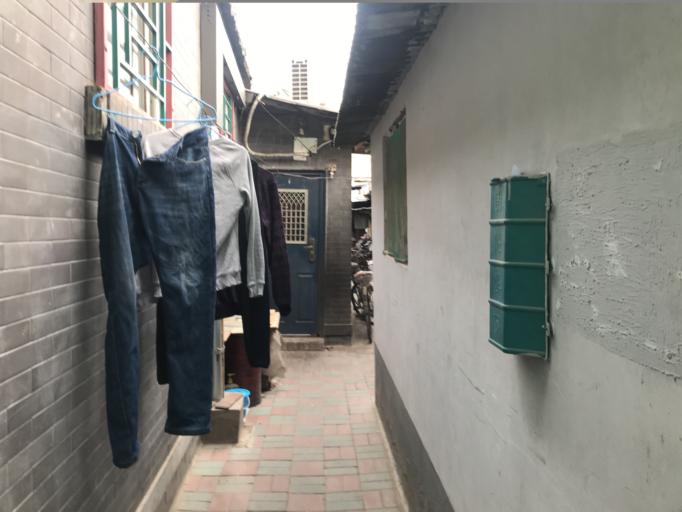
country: CN
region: Beijing
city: Beijing
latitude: 39.8922
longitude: 116.3788
